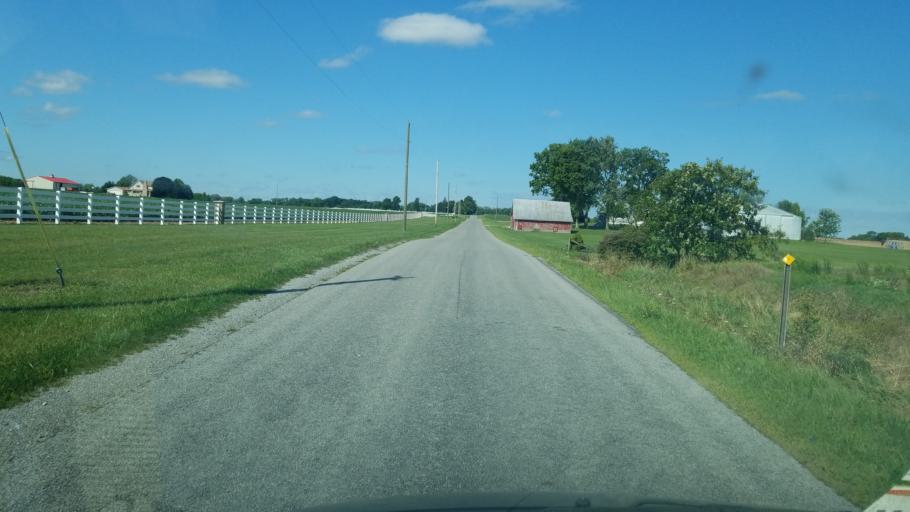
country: US
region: Ohio
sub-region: Wood County
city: North Baltimore
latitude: 41.1242
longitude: -83.6938
